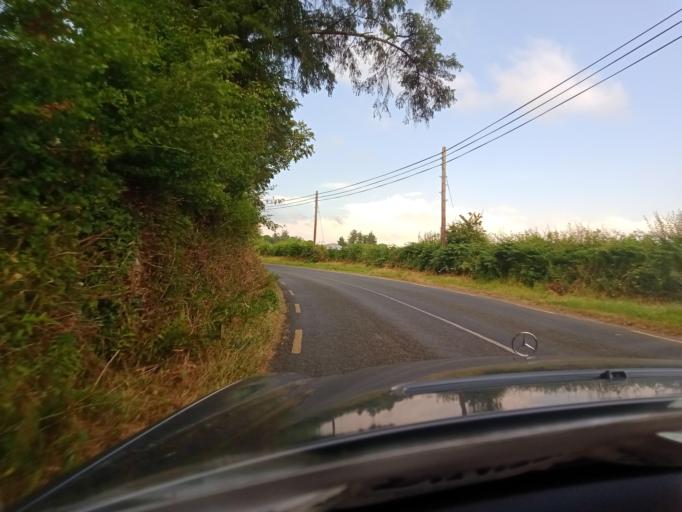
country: IE
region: Leinster
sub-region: Kilkenny
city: Piltown
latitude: 52.4312
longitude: -7.3580
